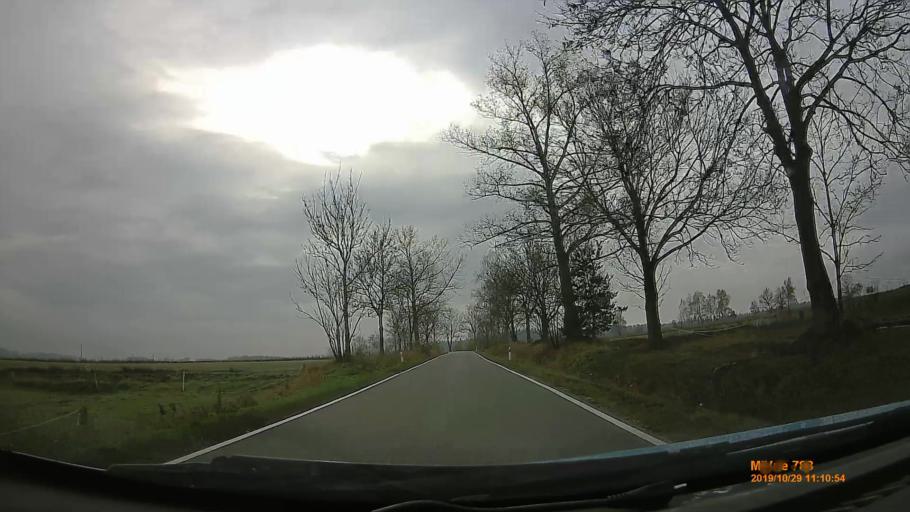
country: PL
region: Lower Silesian Voivodeship
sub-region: Powiat klodzki
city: Polanica-Zdroj
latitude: 50.4395
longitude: 16.5008
